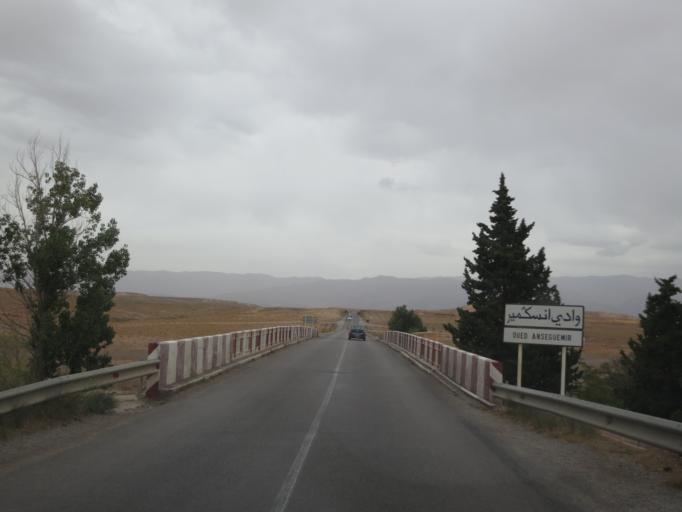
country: MA
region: Meknes-Tafilalet
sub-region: Khenifra
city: Midelt
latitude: 32.7437
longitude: -4.9129
